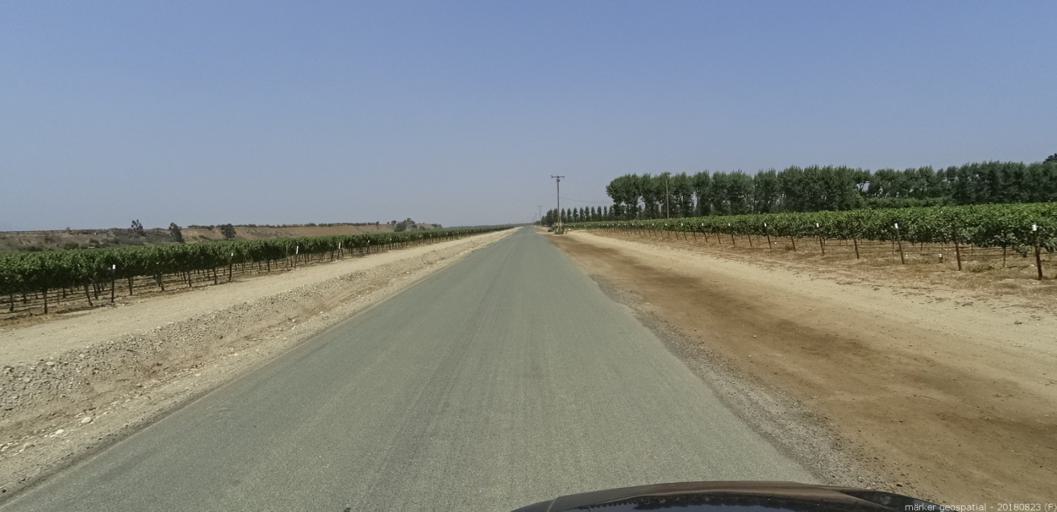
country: US
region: California
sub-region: Monterey County
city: Greenfield
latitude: 36.3435
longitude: -121.2981
